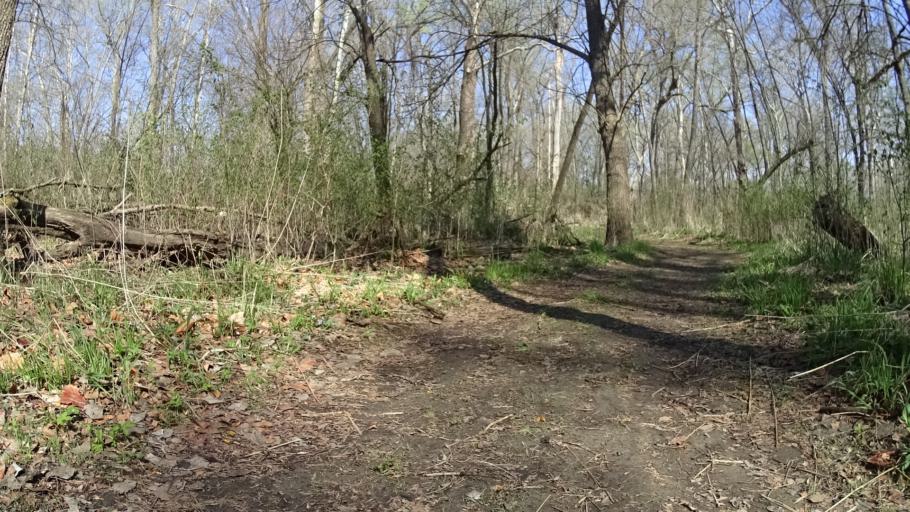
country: US
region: Nebraska
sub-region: Sarpy County
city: Bellevue
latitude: 41.1767
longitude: -95.8920
